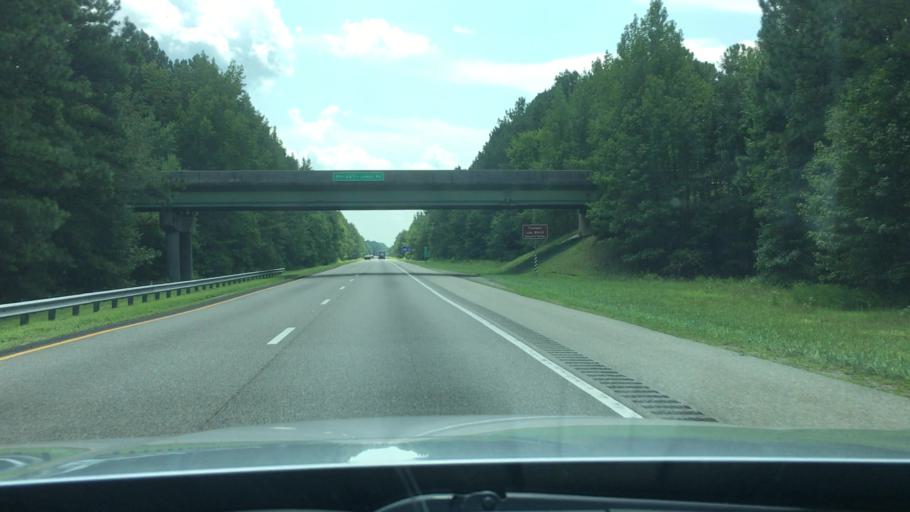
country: US
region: Virginia
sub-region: Sussex County
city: Sussex
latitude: 37.0044
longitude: -77.3925
